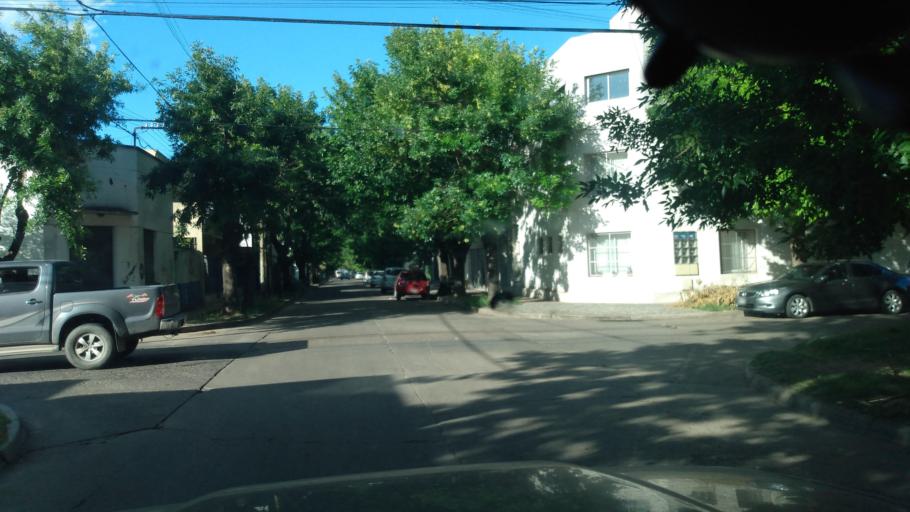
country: AR
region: Buenos Aires
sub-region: Partido de Lujan
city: Lujan
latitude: -34.5668
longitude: -59.1074
